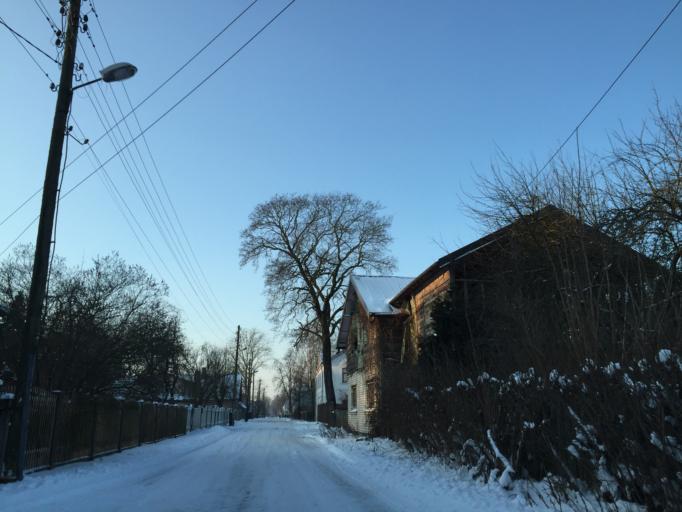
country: LV
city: Tireli
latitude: 56.9450
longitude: 23.6234
